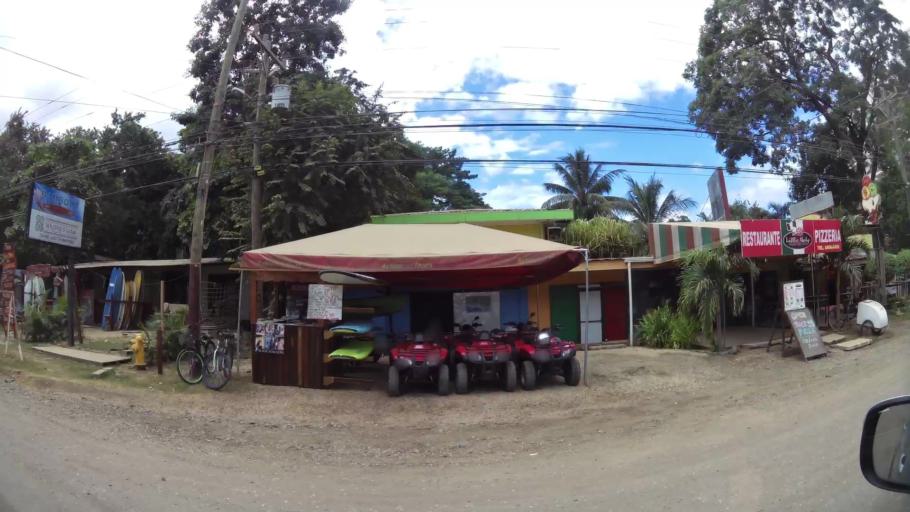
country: CR
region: Guanacaste
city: Santa Cruz
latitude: 10.2973
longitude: -85.8408
